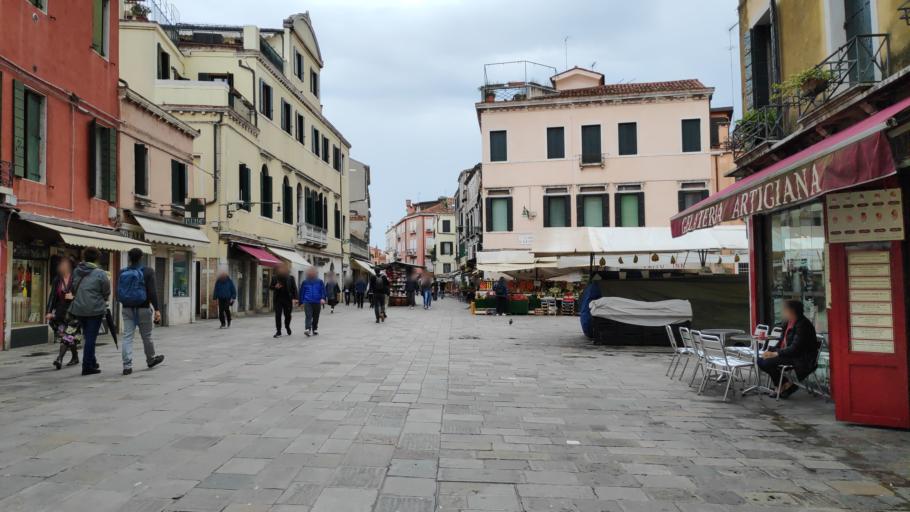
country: IT
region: Veneto
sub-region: Provincia di Venezia
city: Venice
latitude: 45.4437
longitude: 12.3265
